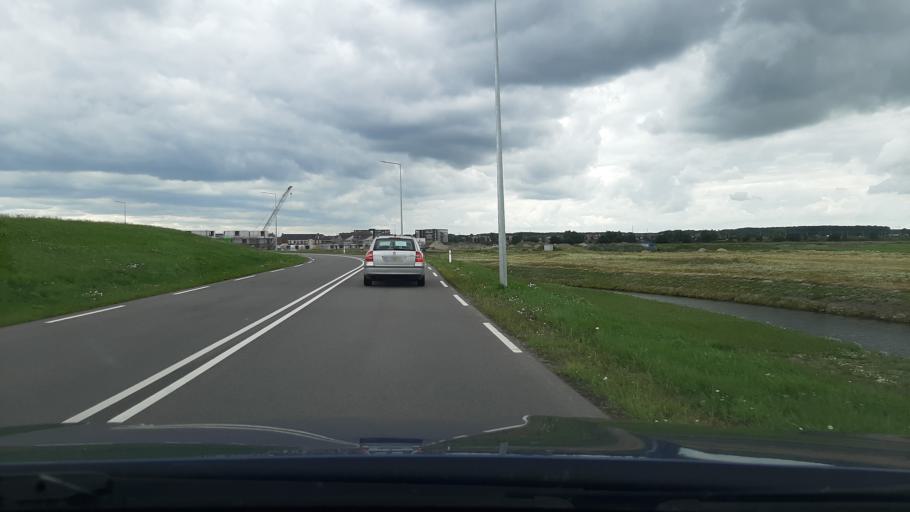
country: NL
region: Flevoland
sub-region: Gemeente Zeewolde
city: Zeewolde
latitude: 52.3511
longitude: 5.5331
